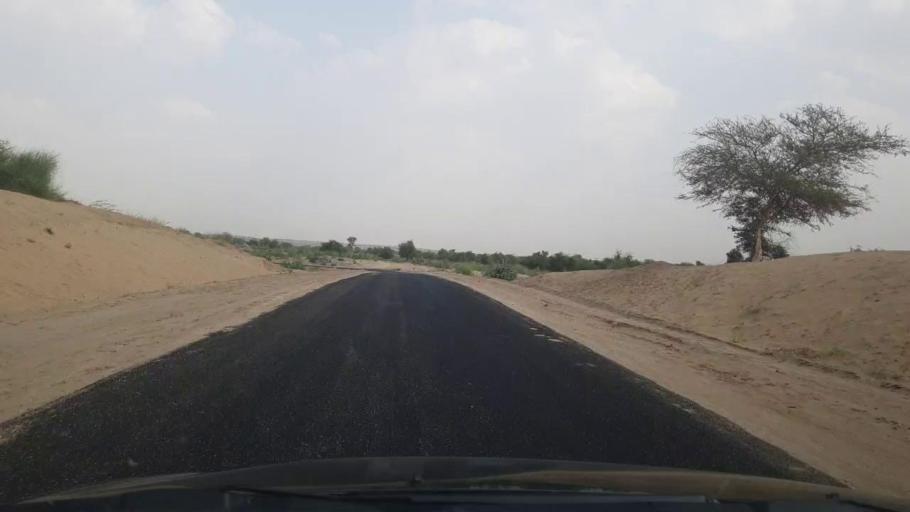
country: PK
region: Sindh
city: Islamkot
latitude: 25.0032
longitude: 70.6655
